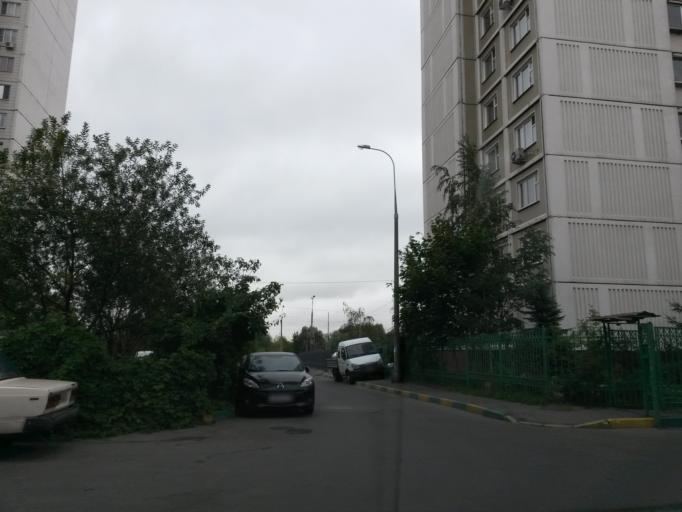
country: RU
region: Moscow
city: Brateyevo
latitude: 55.6524
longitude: 37.7720
